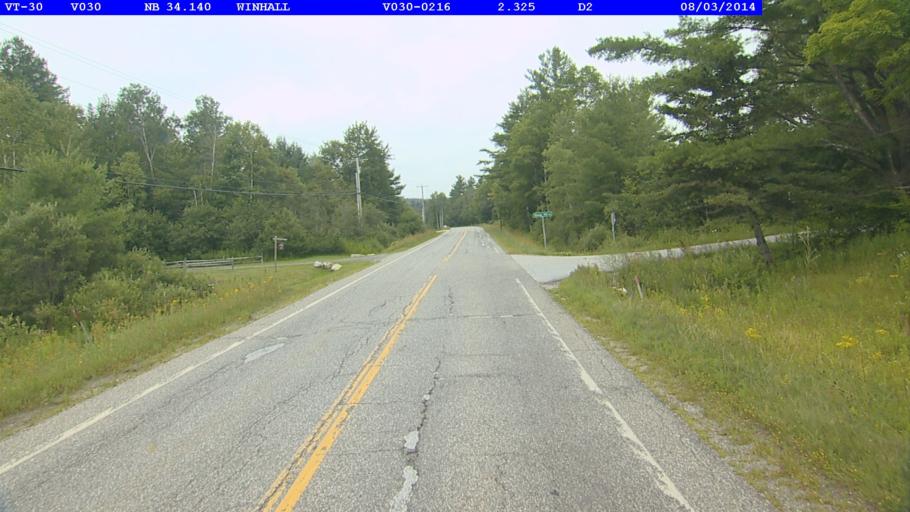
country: US
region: Vermont
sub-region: Bennington County
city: Manchester Center
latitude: 43.1521
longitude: -72.9085
